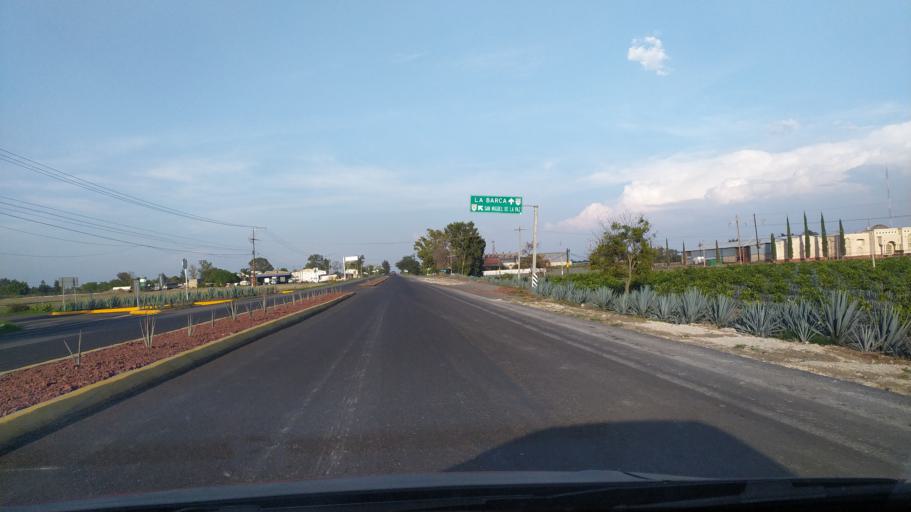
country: MX
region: Jalisco
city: Jamay
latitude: 20.2941
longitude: -102.6734
